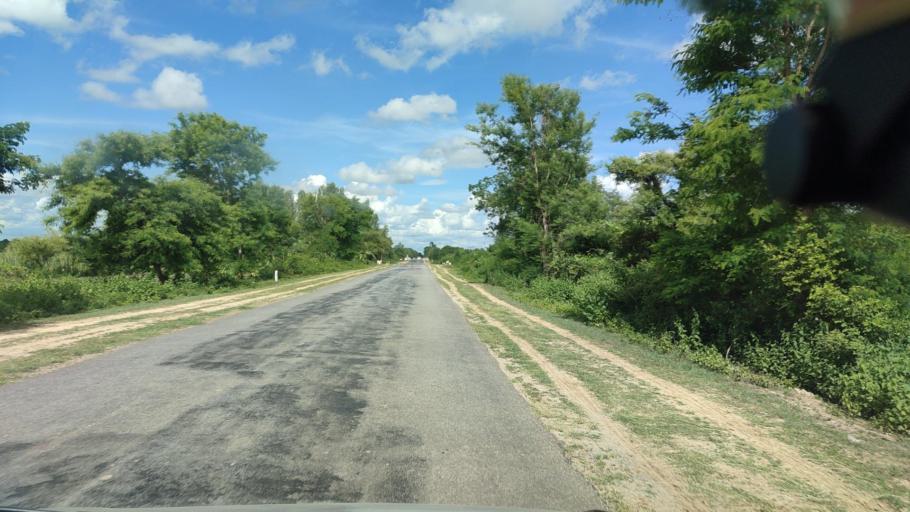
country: MM
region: Magway
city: Taungdwingyi
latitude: 20.1914
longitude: 95.4258
